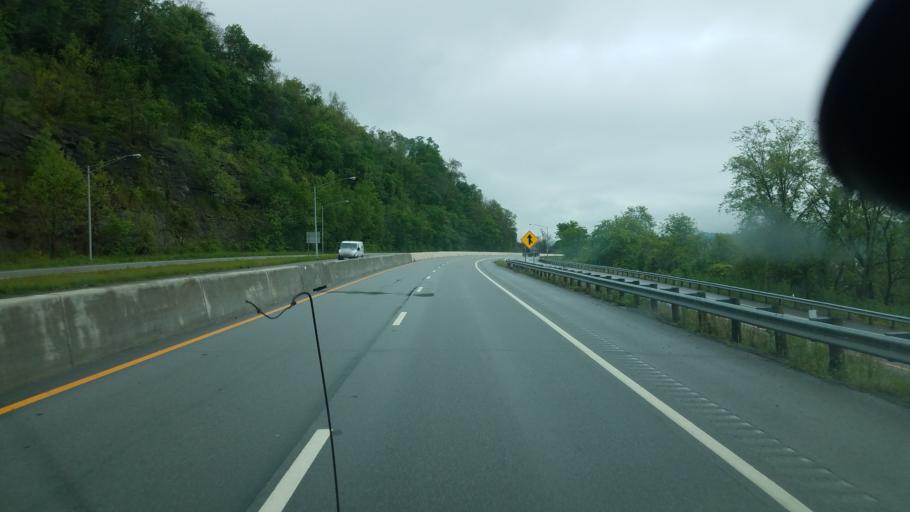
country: US
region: Ohio
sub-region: Jefferson County
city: Tiltonsville
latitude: 40.1759
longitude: -80.6980
